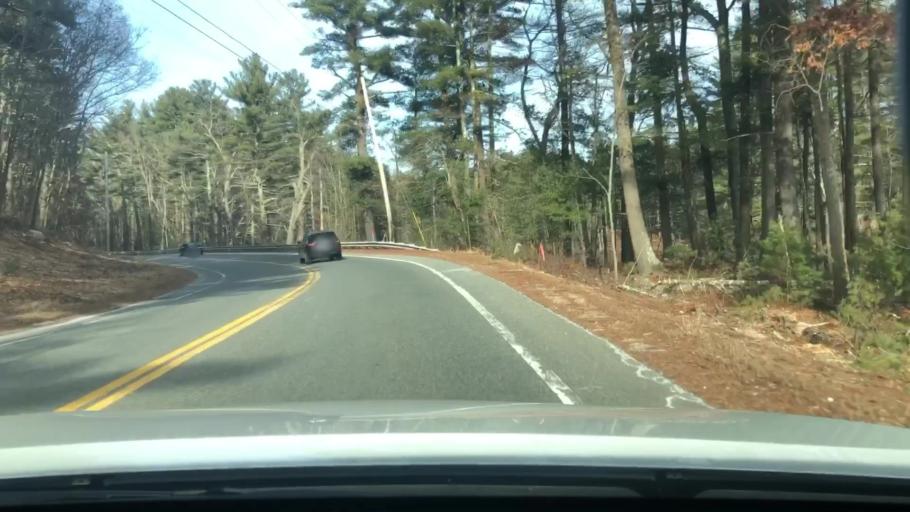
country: US
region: Massachusetts
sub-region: Worcester County
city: Grafton
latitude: 42.1943
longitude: -71.6560
